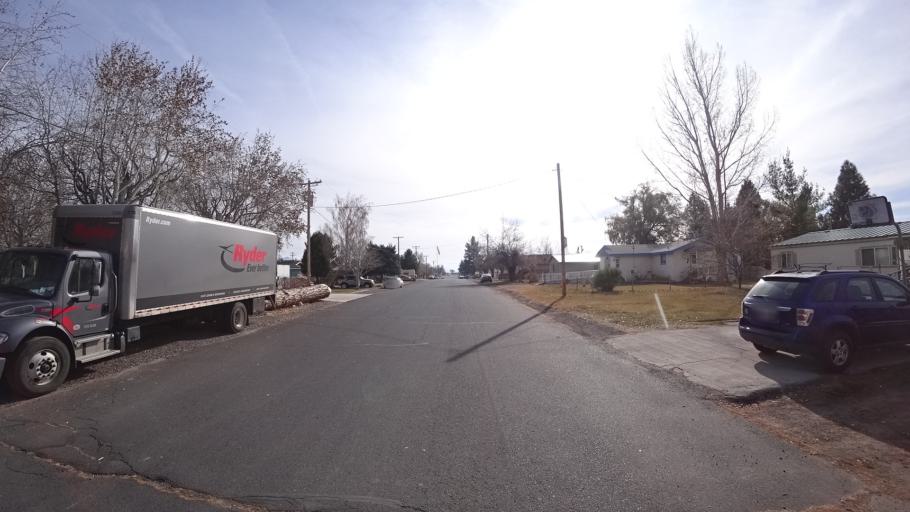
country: US
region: Oregon
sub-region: Klamath County
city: Klamath Falls
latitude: 41.9699
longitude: -121.9184
